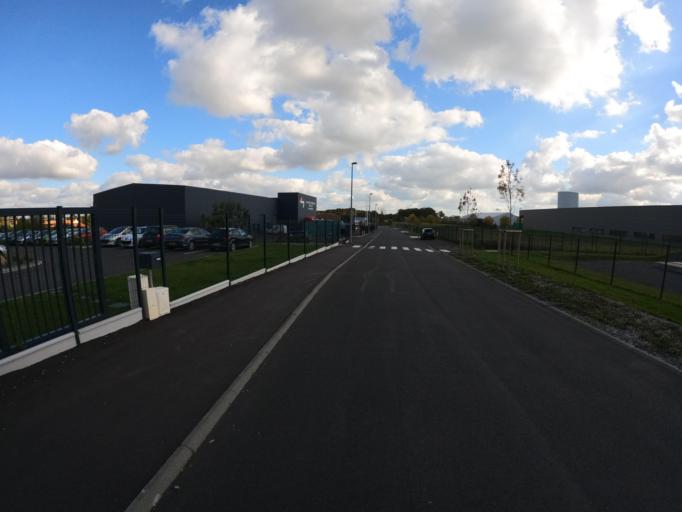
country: FR
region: Pays de la Loire
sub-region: Departement de la Loire-Atlantique
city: Le Bignon
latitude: 47.1009
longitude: -1.4535
